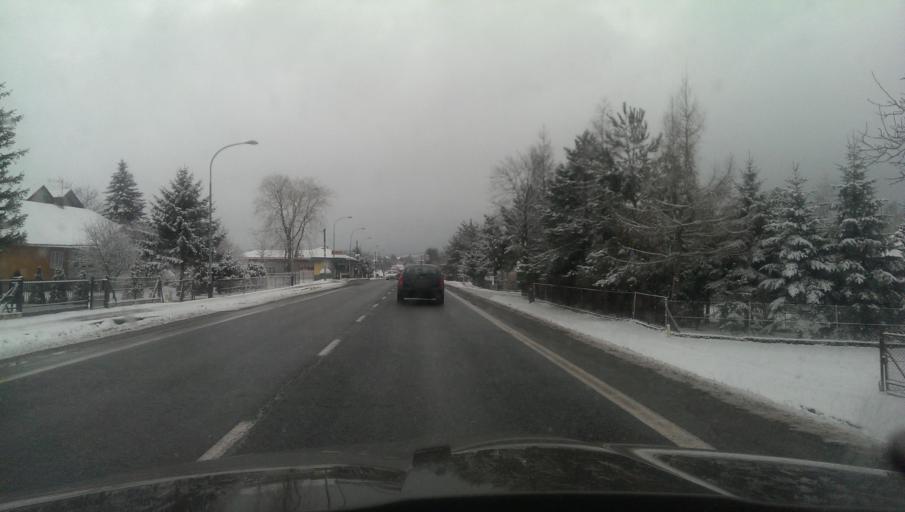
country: PL
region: Subcarpathian Voivodeship
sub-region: Powiat krosnienski
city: Miejsce Piastowe
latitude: 49.6086
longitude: 21.8040
